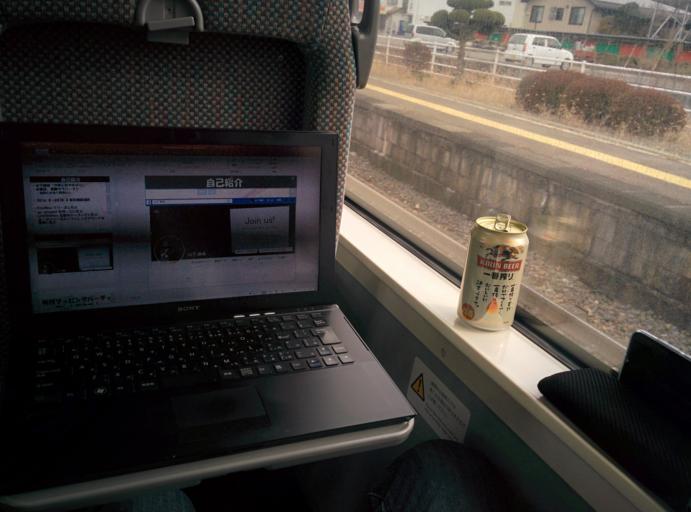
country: JP
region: Nagano
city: Hotaka
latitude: 36.4291
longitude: 138.0133
